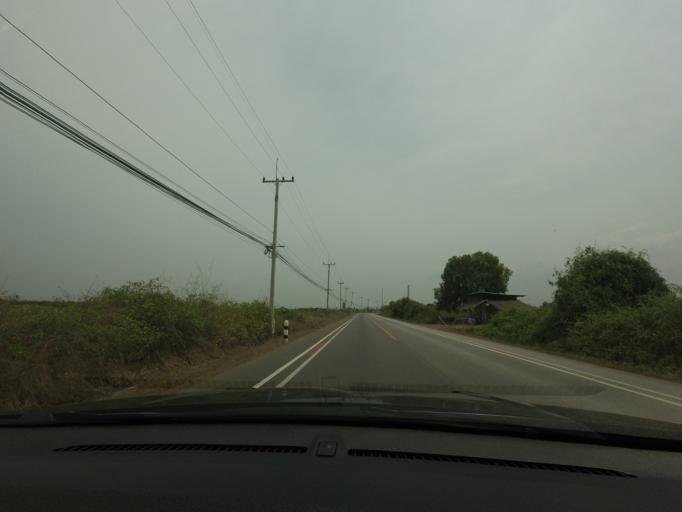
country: TH
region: Ratchaburi
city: Pak Tho
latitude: 13.3235
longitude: 99.9252
